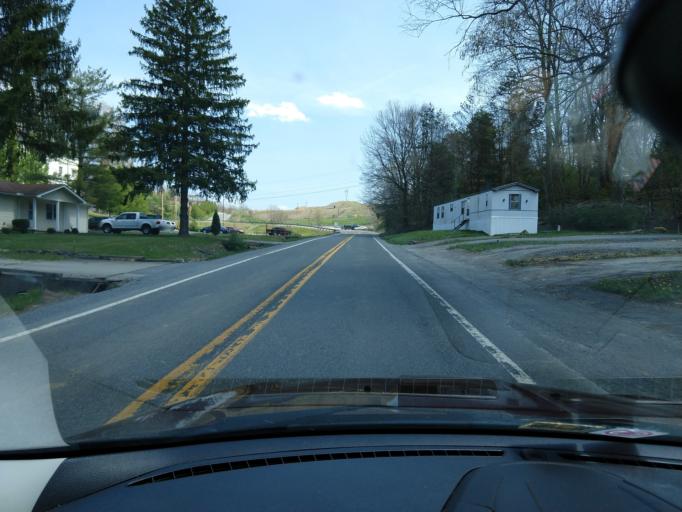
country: US
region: West Virginia
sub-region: Raleigh County
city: Bradley
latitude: 37.8521
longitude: -81.1997
